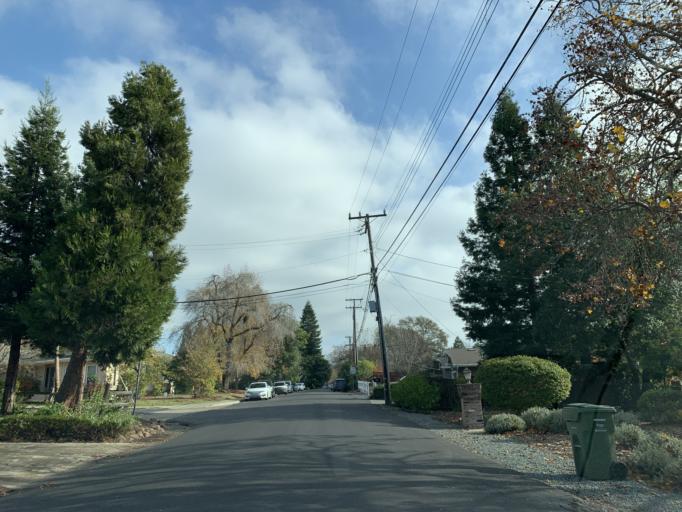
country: US
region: California
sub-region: Contra Costa County
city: Saranap
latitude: 37.8911
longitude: -122.0761
